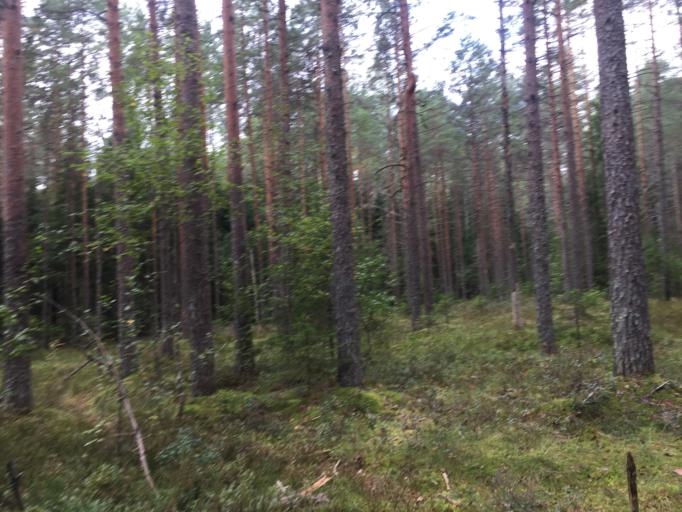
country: RU
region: Leningrad
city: Rozhdestveno
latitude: 59.2939
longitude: 30.0068
